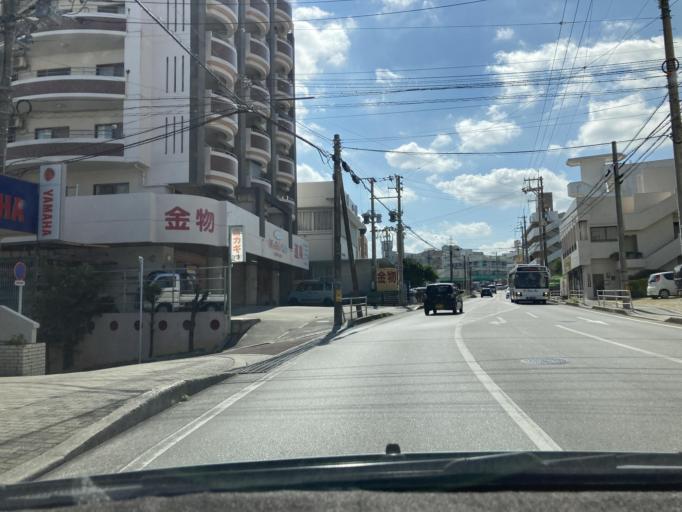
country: JP
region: Okinawa
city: Tomigusuku
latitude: 26.1922
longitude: 127.6783
